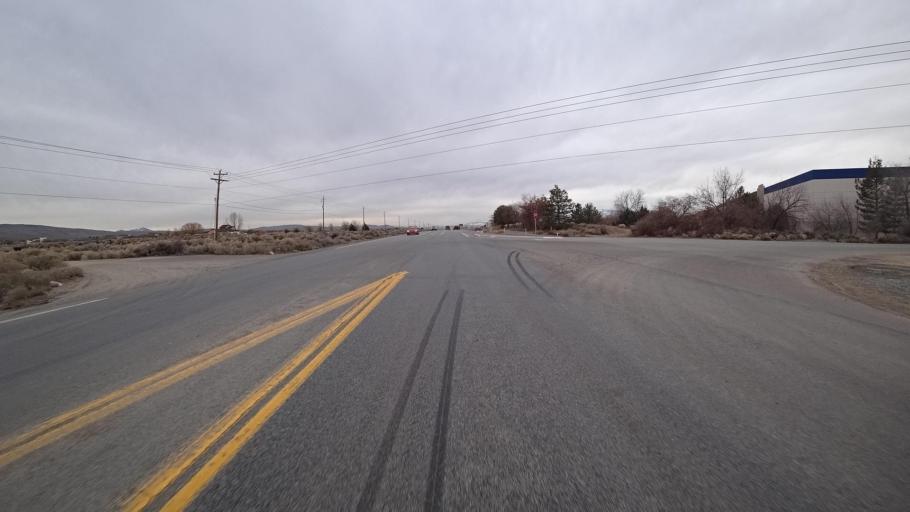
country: US
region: Nevada
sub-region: Washoe County
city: Spanish Springs
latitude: 39.6733
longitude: -119.7018
